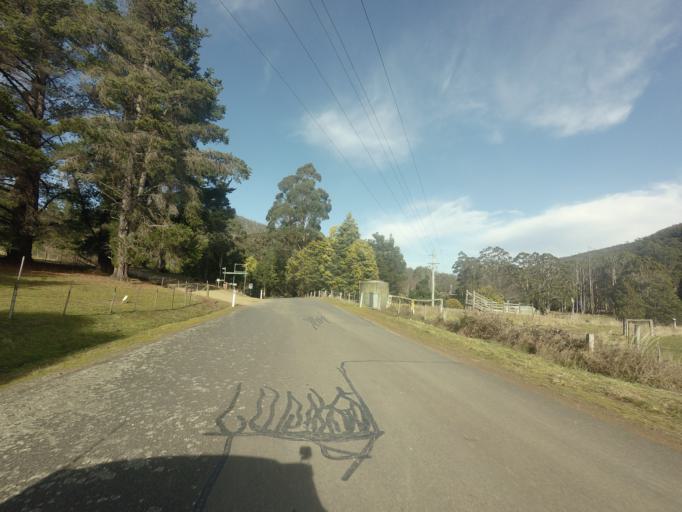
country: AU
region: Tasmania
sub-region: Huon Valley
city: Huonville
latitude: -43.0483
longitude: 147.1108
